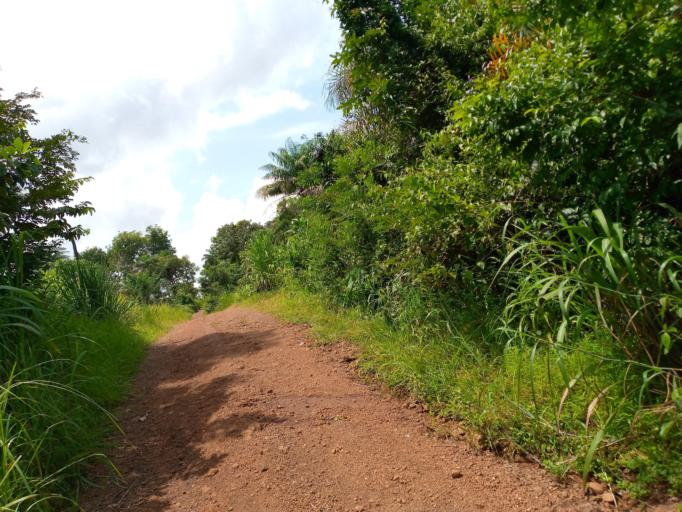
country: SL
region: Northern Province
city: Binkolo
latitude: 9.1179
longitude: -12.1340
